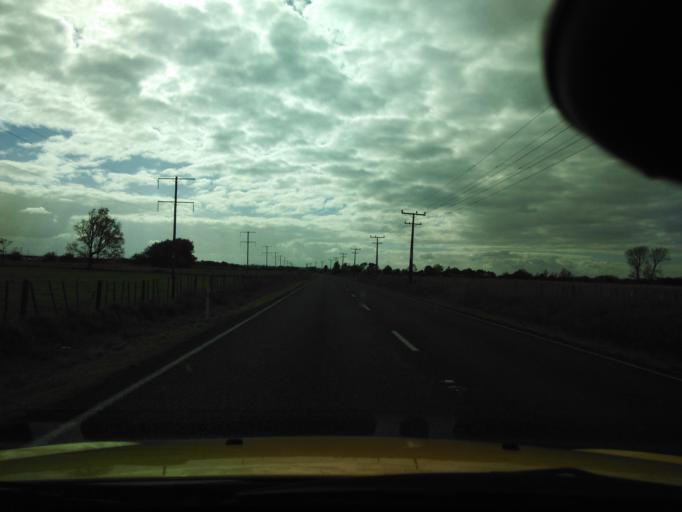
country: NZ
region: Waikato
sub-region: Waikato District
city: Te Kauwhata
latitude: -37.4848
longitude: 175.1457
